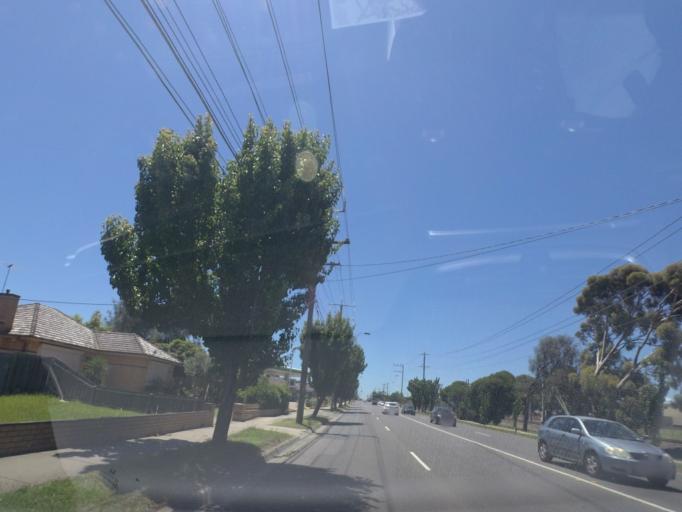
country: AU
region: Victoria
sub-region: Whittlesea
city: Thomastown
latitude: -37.6845
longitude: 145.0131
